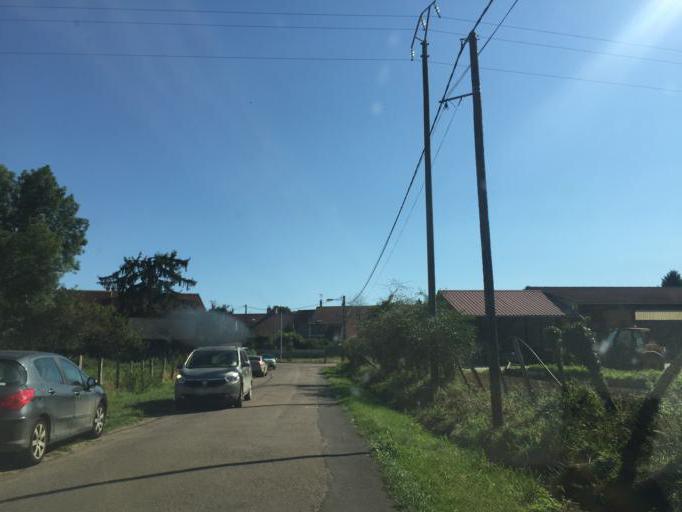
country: FR
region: Bourgogne
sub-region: Departement de l'Yonne
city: Fontenailles
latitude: 47.5057
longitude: 3.3459
